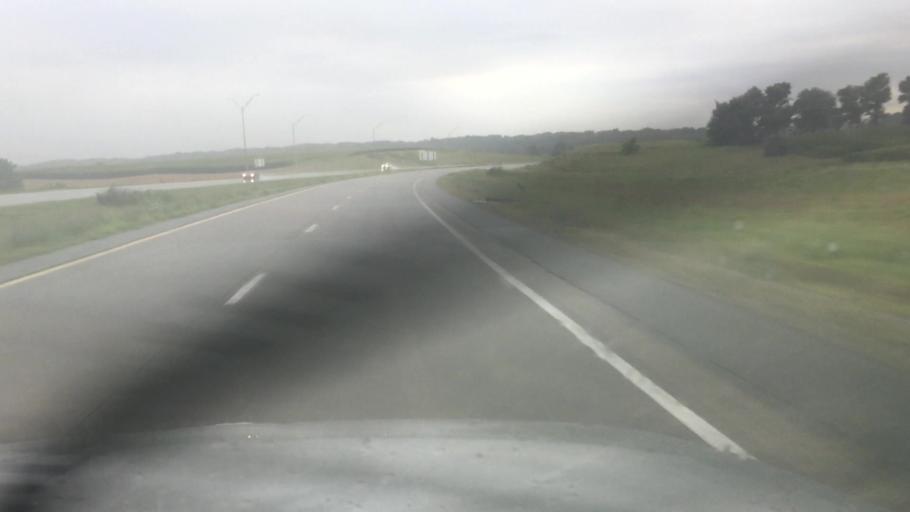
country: US
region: Iowa
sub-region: Washington County
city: Washington
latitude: 41.2883
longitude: -91.5331
